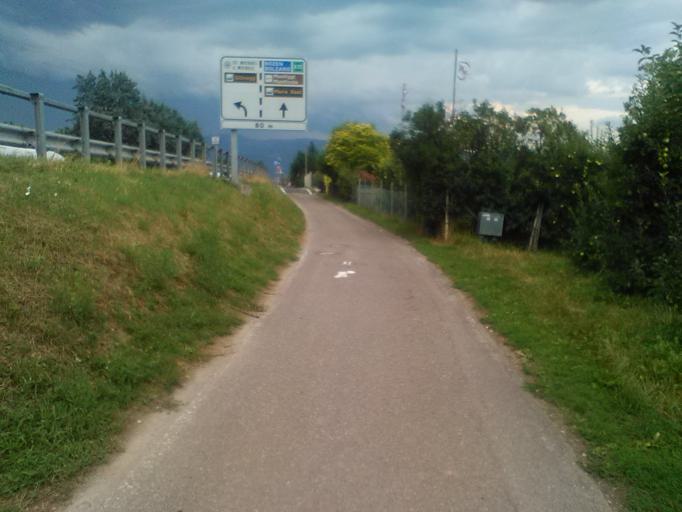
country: IT
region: Trentino-Alto Adige
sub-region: Bolzano
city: San Michele
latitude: 46.4470
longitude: 11.2644
